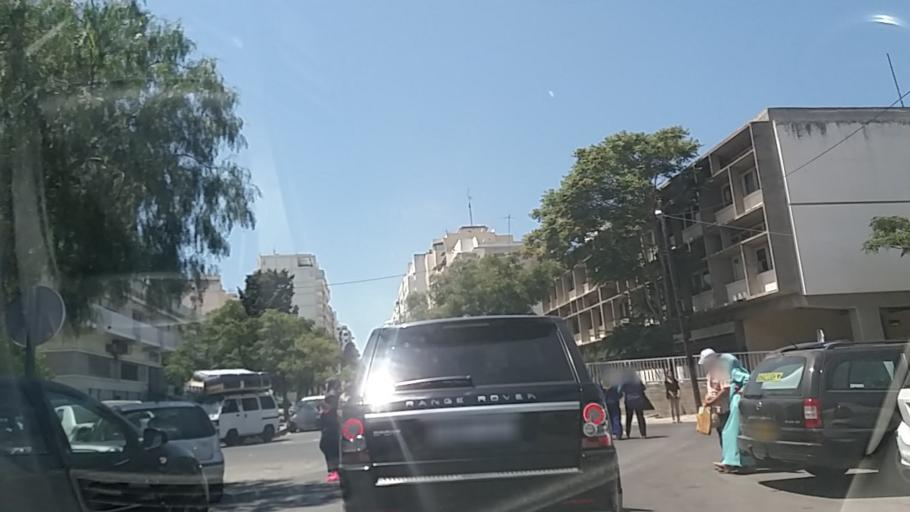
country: MA
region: Tanger-Tetouan
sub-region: Tanger-Assilah
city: Tangier
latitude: 35.7751
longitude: -5.8069
